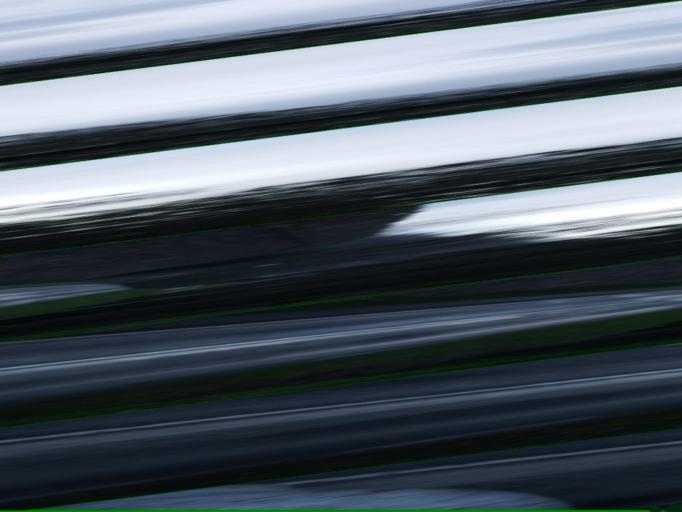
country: FR
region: Picardie
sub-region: Departement de l'Oise
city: Chaumont-en-Vexin
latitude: 49.2714
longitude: 1.8726
